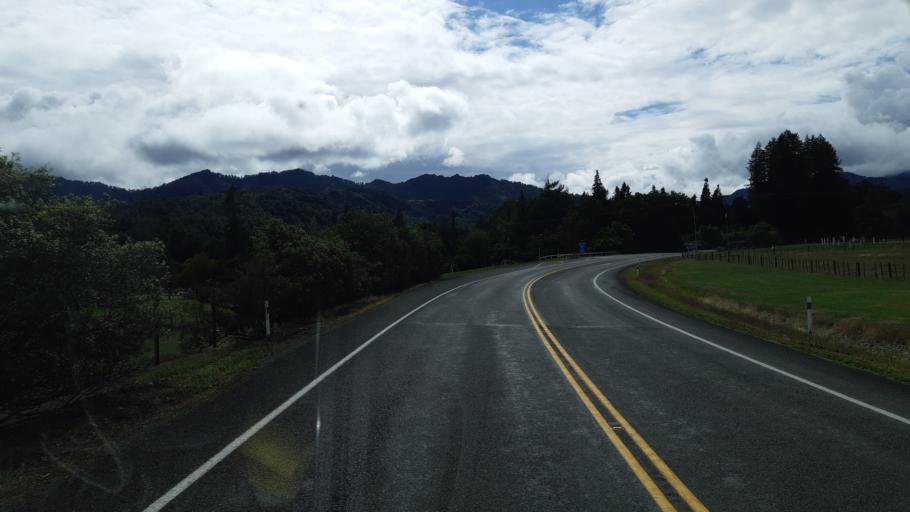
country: NZ
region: West Coast
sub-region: Buller District
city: Westport
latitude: -41.7976
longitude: 172.3382
